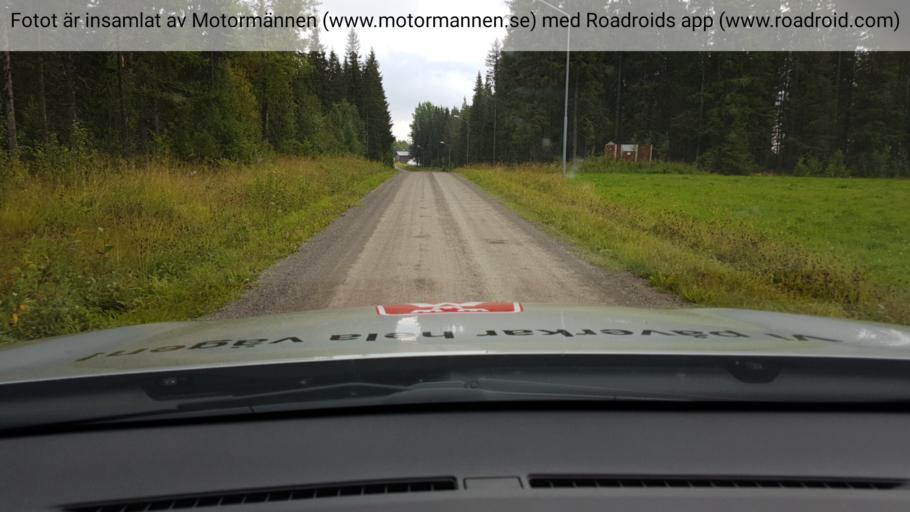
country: SE
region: Jaemtland
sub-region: Stroemsunds Kommun
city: Stroemsund
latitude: 63.7731
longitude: 15.3232
